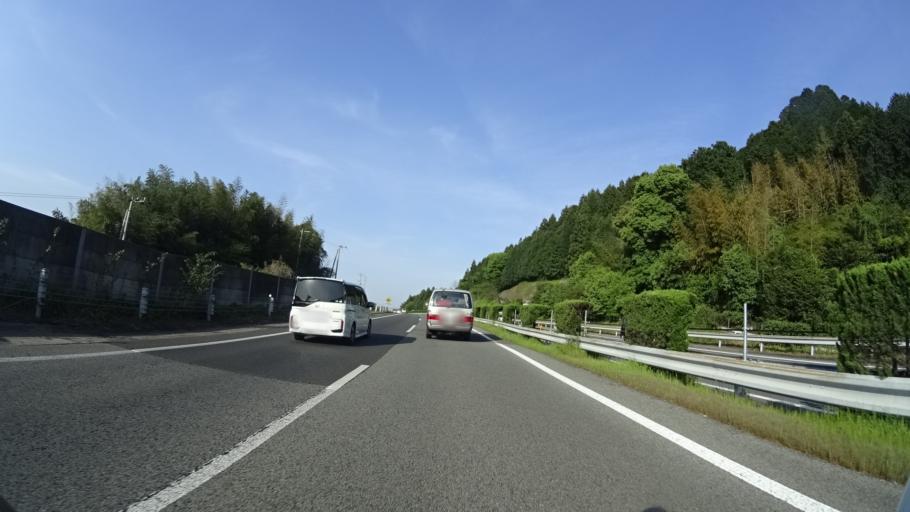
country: JP
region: Ehime
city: Niihama
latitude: 33.9364
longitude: 133.3782
